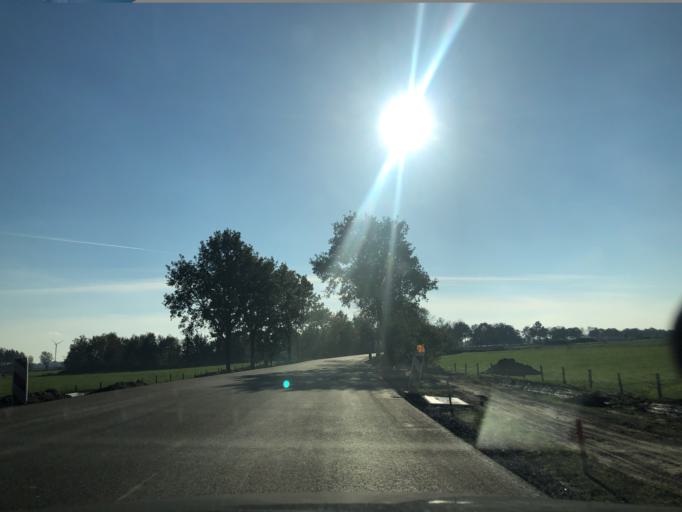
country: DE
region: Lower Saxony
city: Lemwerder
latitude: 53.1610
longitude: 8.5590
